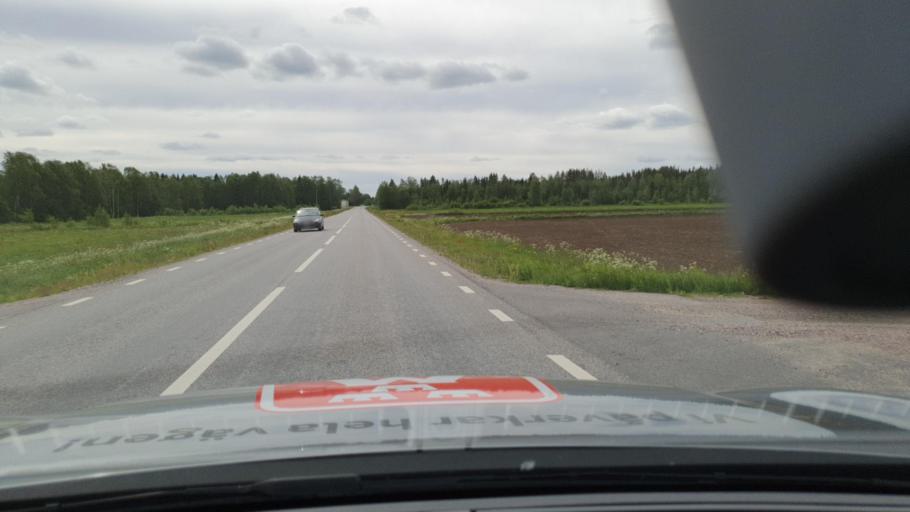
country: SE
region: Norrbotten
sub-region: Kalix Kommun
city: Kalix
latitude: 65.9382
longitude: 23.4603
